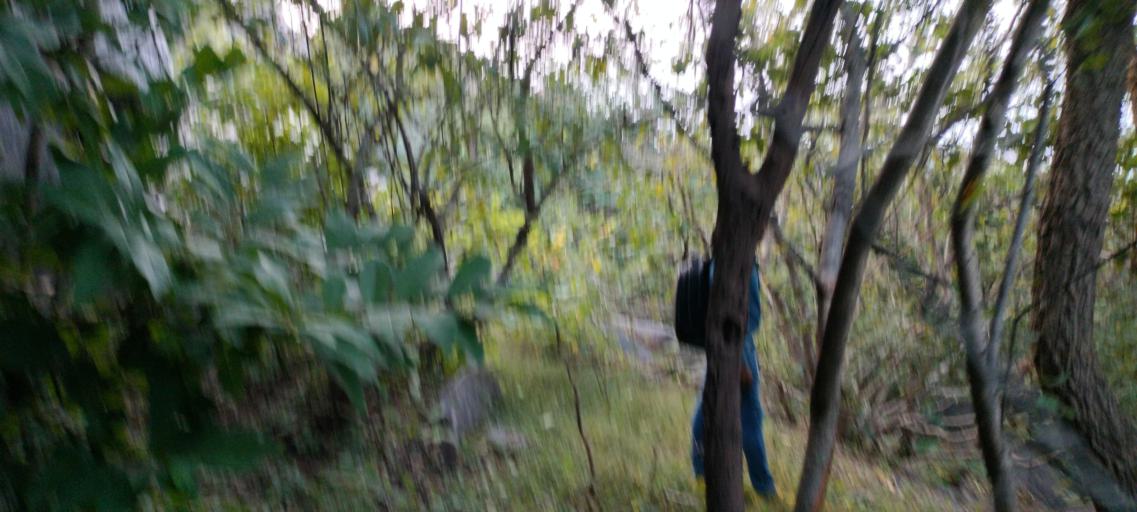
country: IN
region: Telangana
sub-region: Mahbubnagar
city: Farrukhnagar
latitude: 16.8963
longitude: 78.4936
